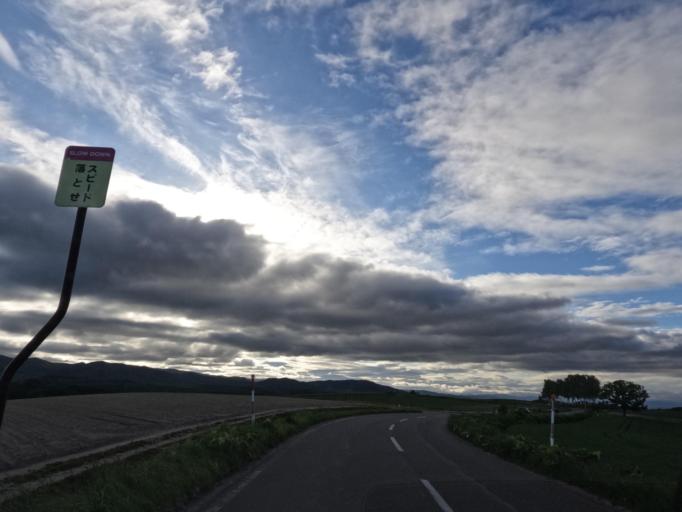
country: JP
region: Hokkaido
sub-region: Asahikawa-shi
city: Asahikawa
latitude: 43.6276
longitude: 142.4321
